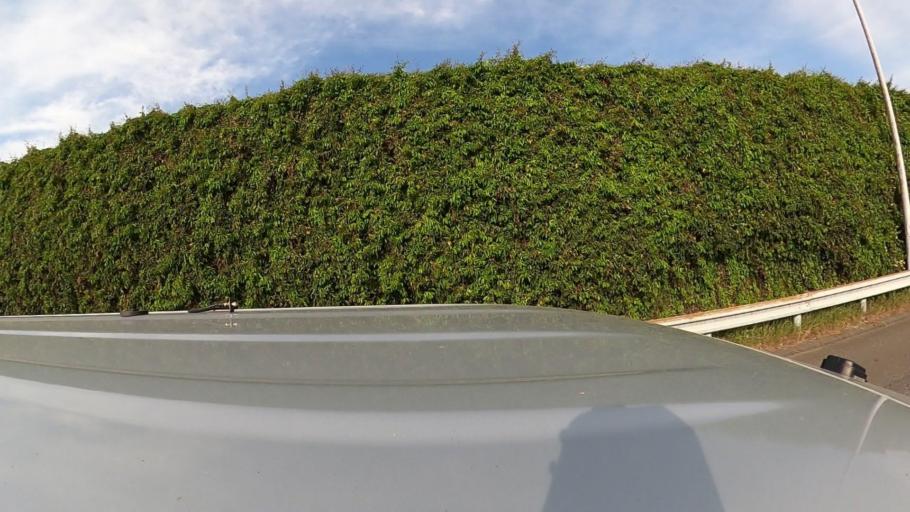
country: JP
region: Saitama
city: Oi
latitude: 35.8501
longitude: 139.5015
